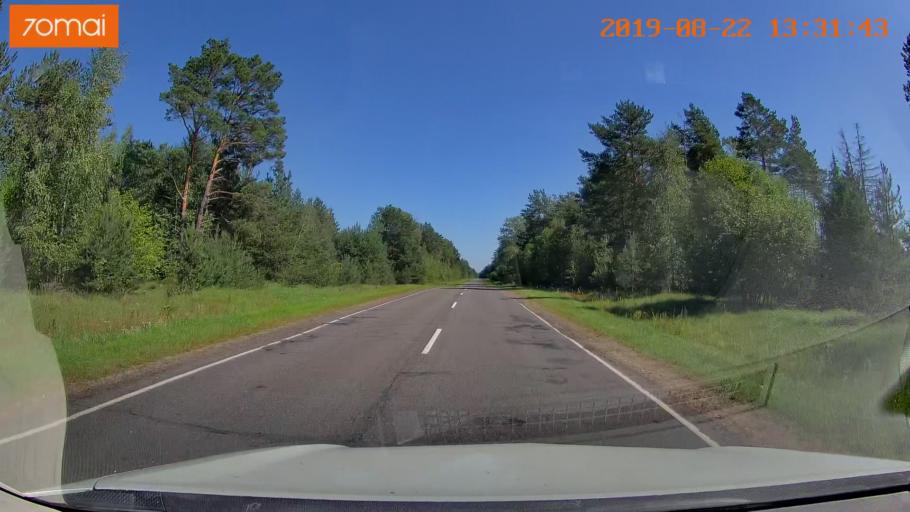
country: BY
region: Minsk
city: Staryya Darohi
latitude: 53.2172
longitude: 28.1861
